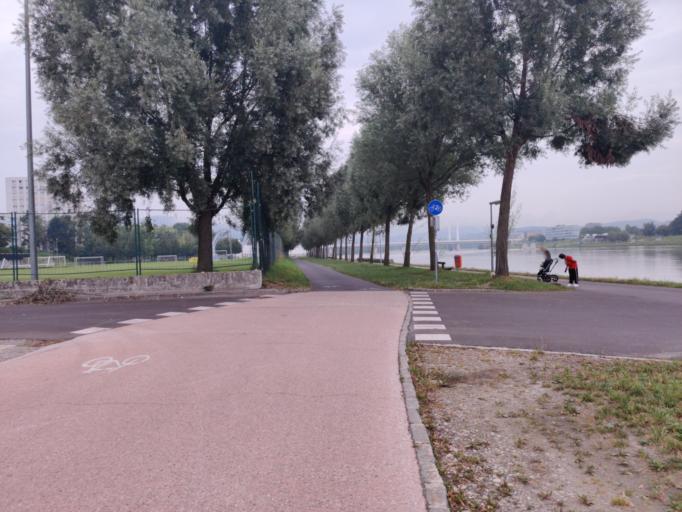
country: AT
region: Upper Austria
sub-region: Linz Stadt
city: Linz
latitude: 48.3142
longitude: 14.2905
